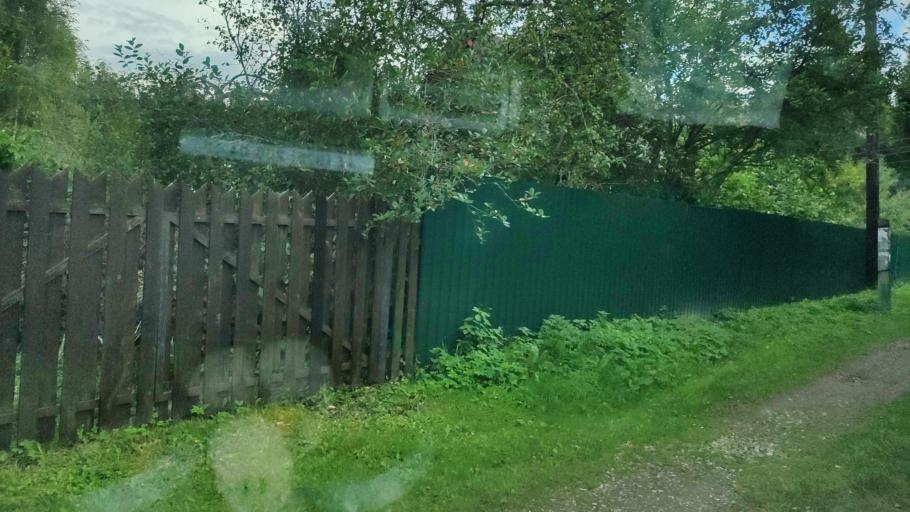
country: RU
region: Moskovskaya
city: Khot'kovo
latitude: 56.2088
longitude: 37.9801
